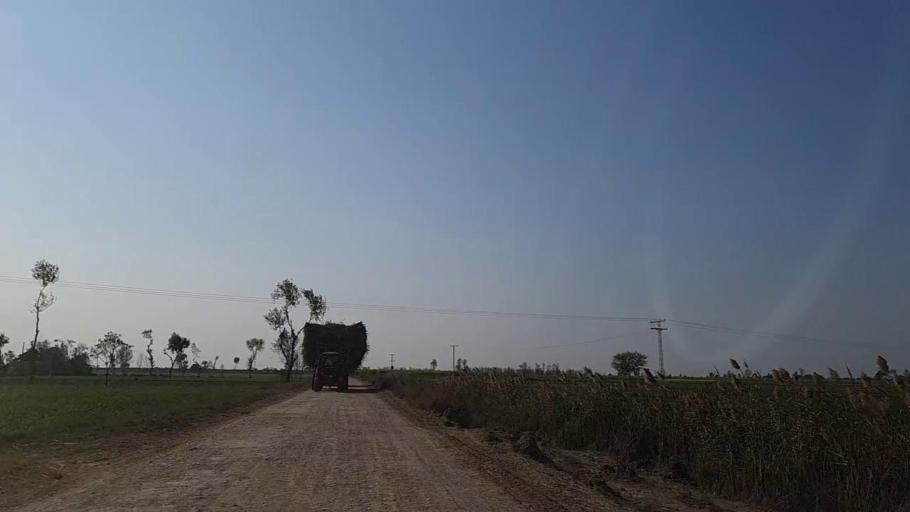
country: PK
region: Sindh
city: Daur
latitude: 26.4713
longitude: 68.2997
